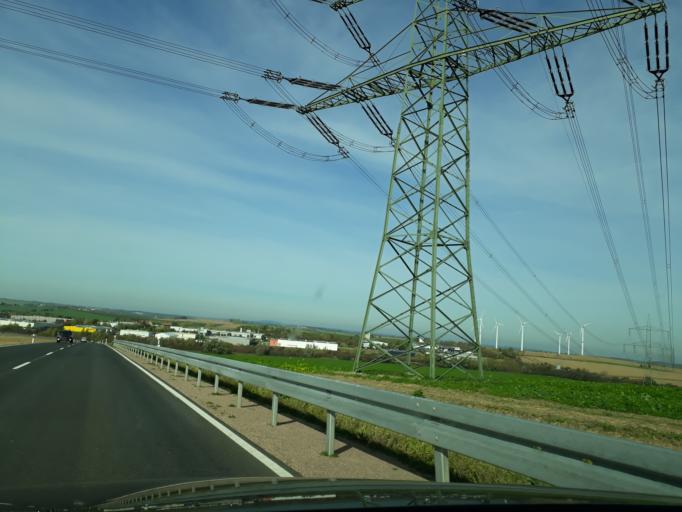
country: DE
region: Saxony
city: Mochau
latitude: 51.1136
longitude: 13.1713
